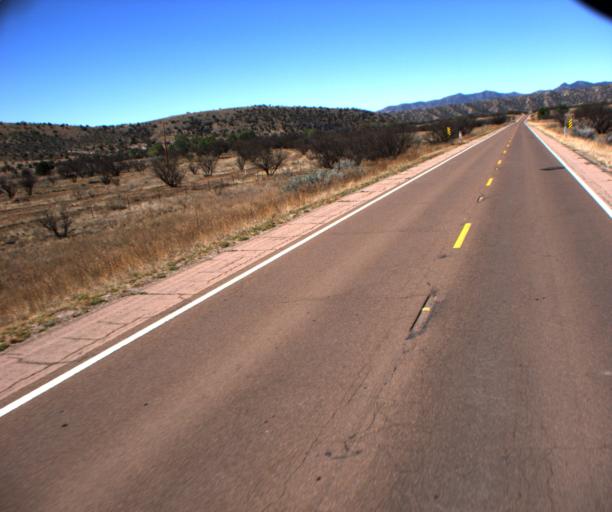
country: US
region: Arizona
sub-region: Pima County
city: Corona de Tucson
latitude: 31.6600
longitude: -110.6922
